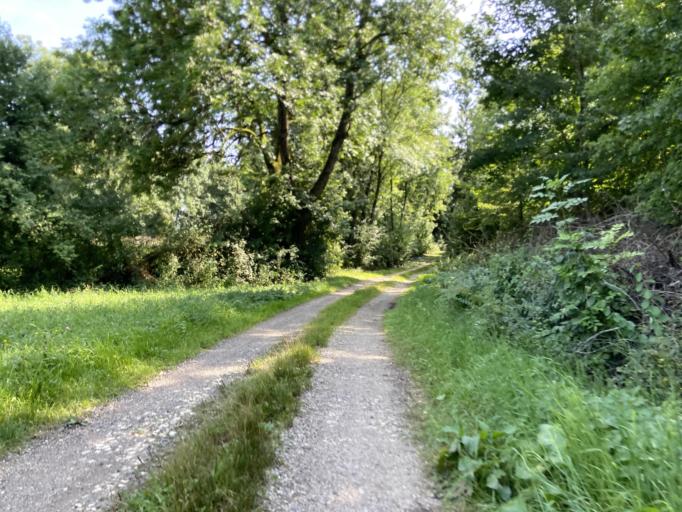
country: DE
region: Baden-Wuerttemberg
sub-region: Tuebingen Region
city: Scheer
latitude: 48.0801
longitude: 9.2787
